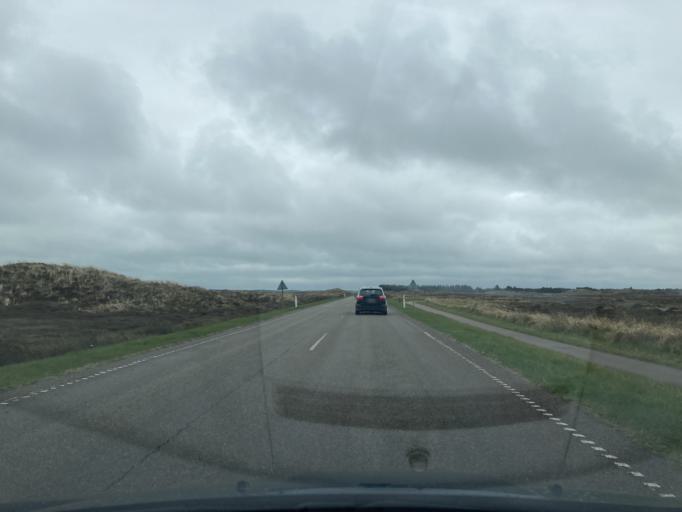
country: DK
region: North Denmark
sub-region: Thisted Kommune
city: Hanstholm
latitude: 57.0158
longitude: 8.4718
